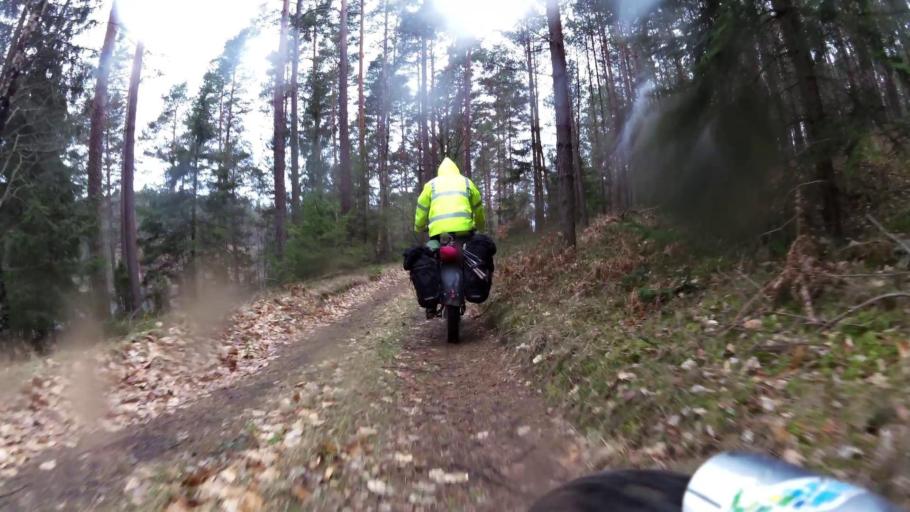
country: PL
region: Pomeranian Voivodeship
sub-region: Powiat bytowski
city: Trzebielino
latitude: 54.0770
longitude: 17.1086
